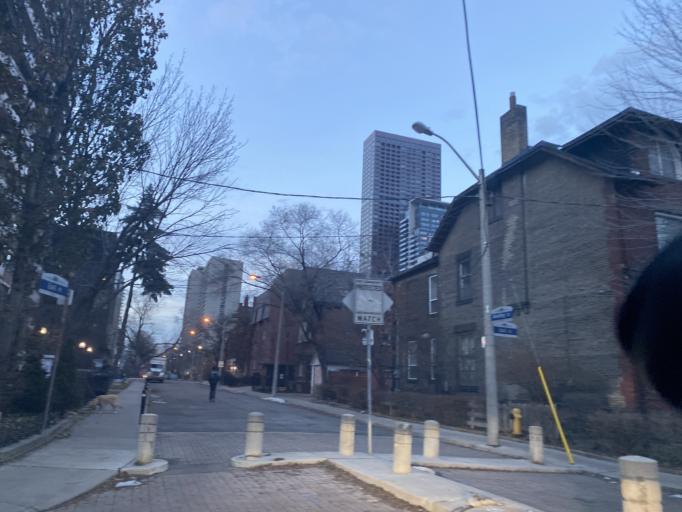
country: CA
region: Ontario
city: Toronto
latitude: 43.6682
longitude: -79.3778
